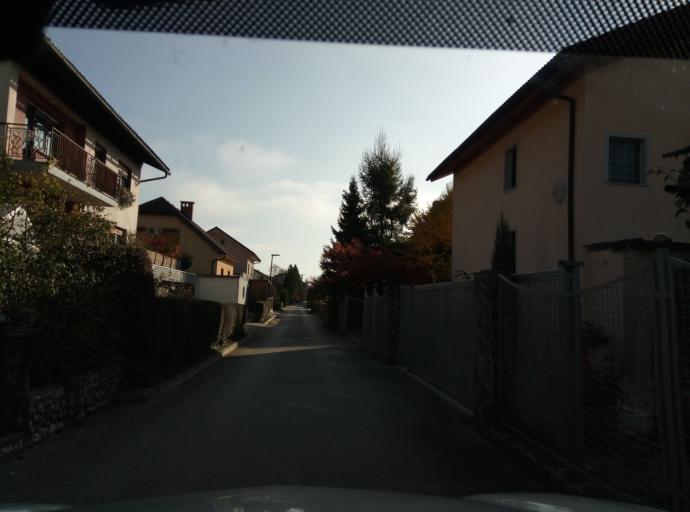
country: SI
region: Medvode
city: Zgornje Pirnice
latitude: 46.1195
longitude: 14.4574
